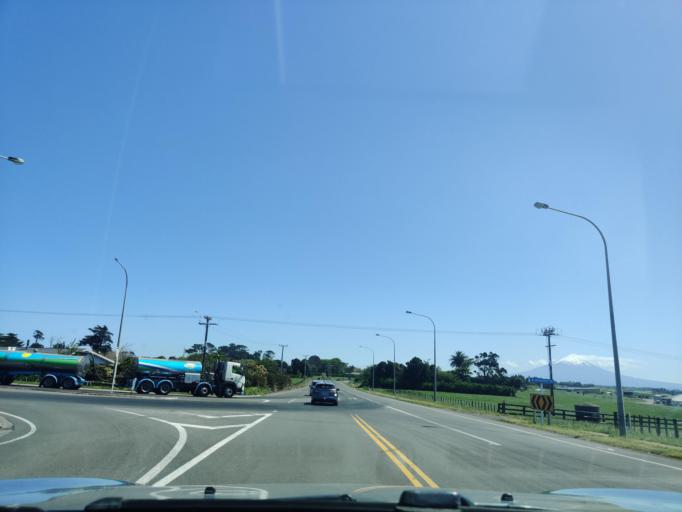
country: NZ
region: Taranaki
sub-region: South Taranaki District
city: Hawera
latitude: -39.6029
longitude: 174.3094
